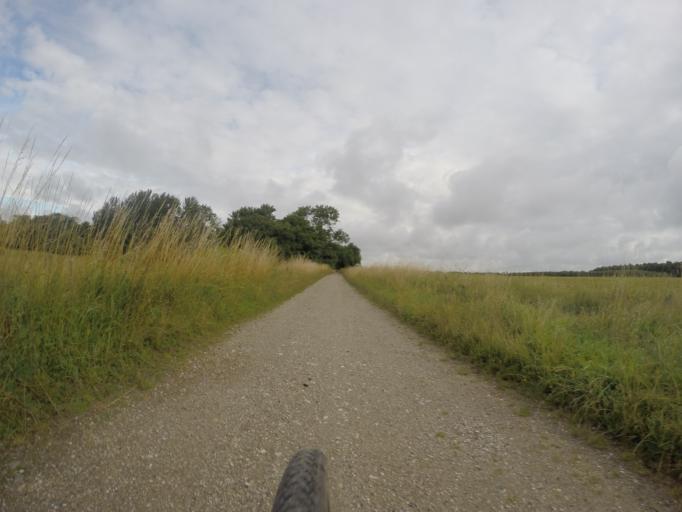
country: DK
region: Capital Region
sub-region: Hoje-Taastrup Kommune
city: Taastrup
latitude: 55.6910
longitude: 12.3186
